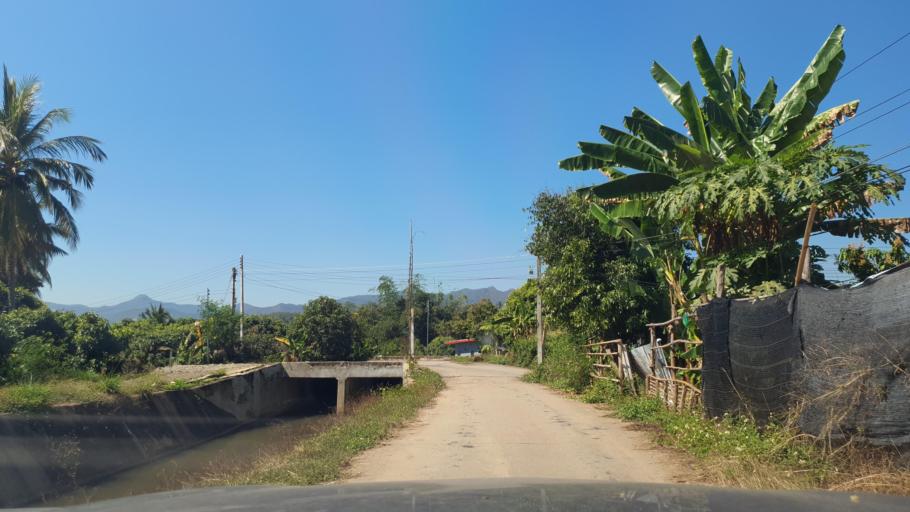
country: TH
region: Chiang Mai
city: Mae Wang
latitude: 18.6777
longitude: 98.8186
